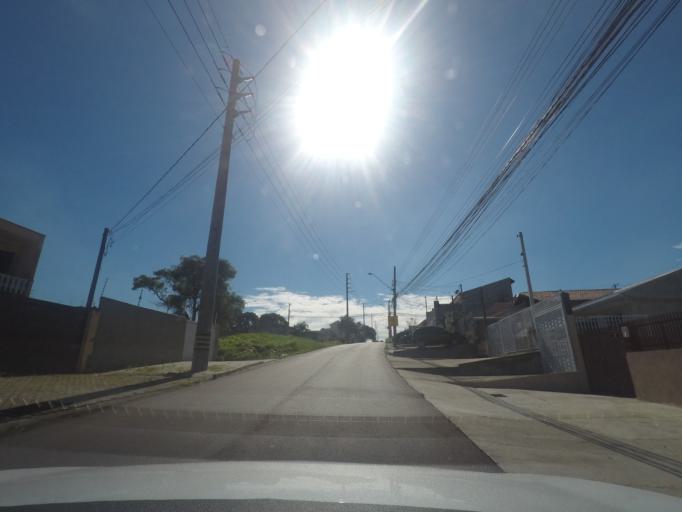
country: BR
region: Parana
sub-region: Sao Jose Dos Pinhais
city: Sao Jose dos Pinhais
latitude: -25.5052
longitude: -49.2780
